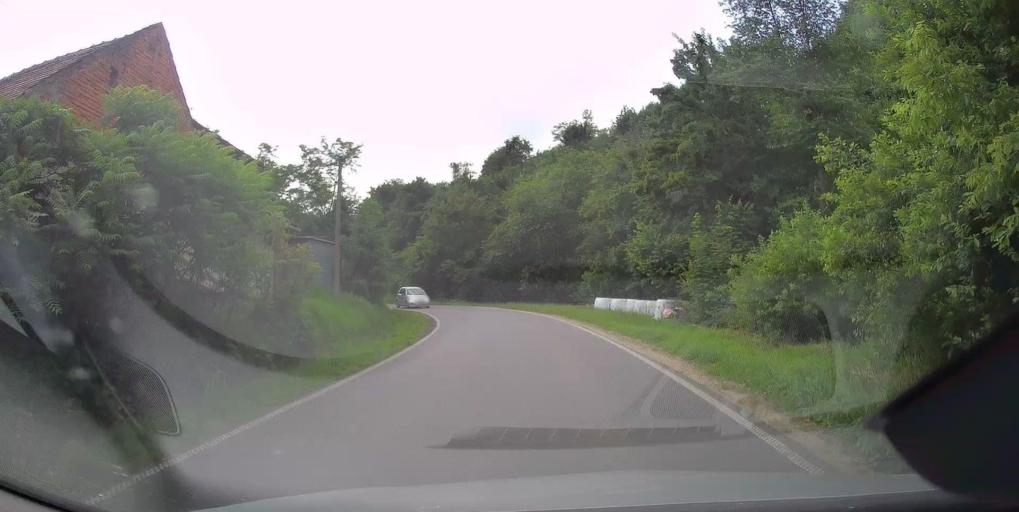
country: PL
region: Lesser Poland Voivodeship
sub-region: Powiat nowosadecki
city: Korzenna
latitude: 49.7217
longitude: 20.7740
